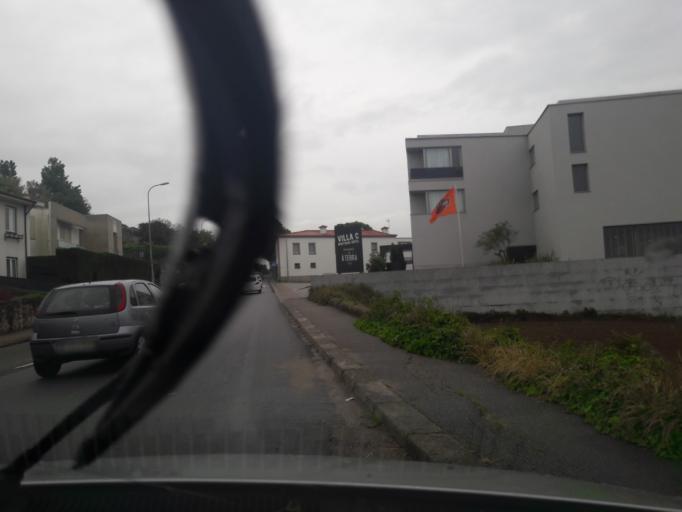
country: PT
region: Porto
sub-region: Vila do Conde
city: Vila do Conde
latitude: 41.3474
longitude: -8.7384
